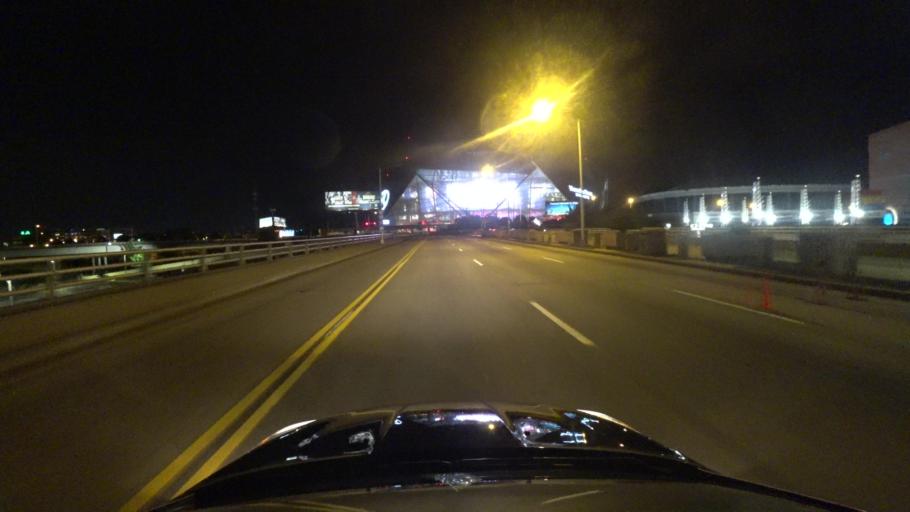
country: US
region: Georgia
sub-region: Fulton County
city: Atlanta
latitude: 33.7564
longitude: -84.3960
